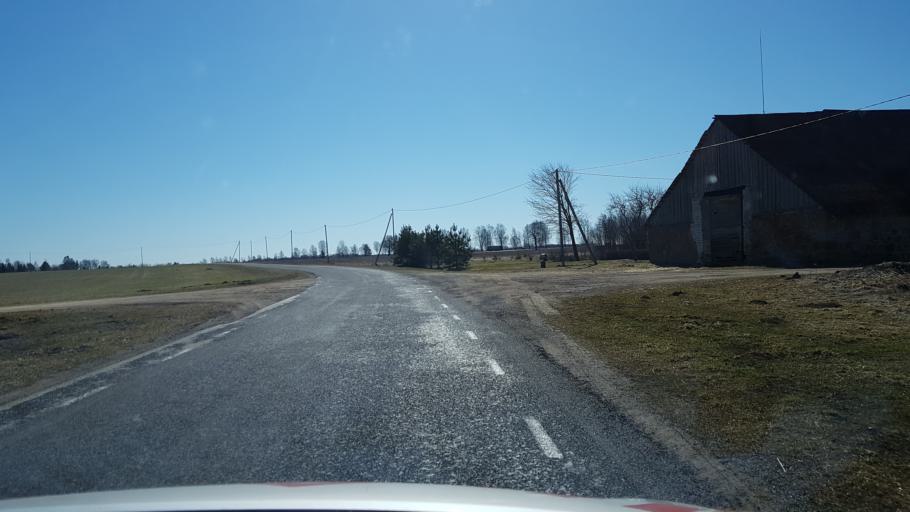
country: EE
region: Laeaene-Virumaa
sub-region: Haljala vald
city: Haljala
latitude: 59.4379
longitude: 26.1737
